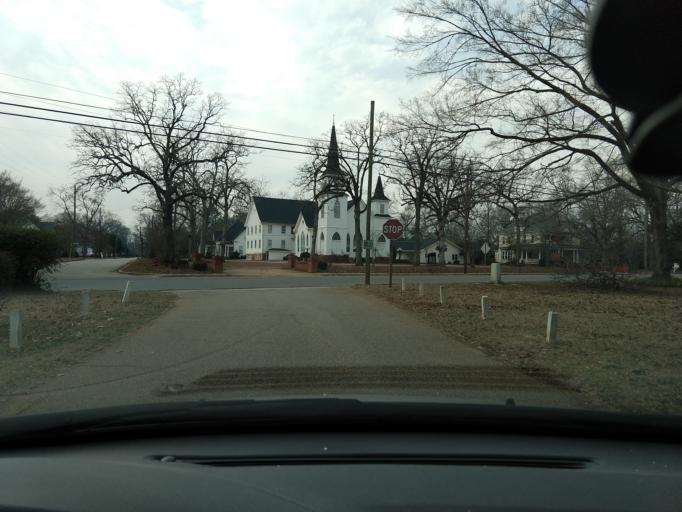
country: US
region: Georgia
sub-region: Webster County
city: Preston
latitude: 32.0365
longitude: -84.3932
